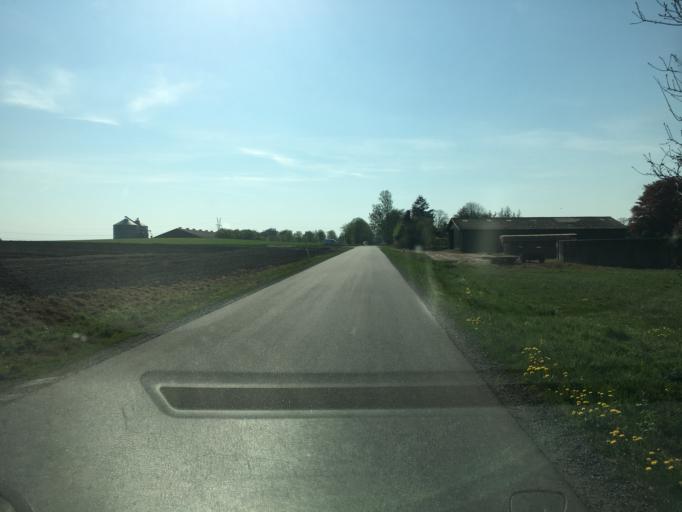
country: DK
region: South Denmark
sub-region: Haderslev Kommune
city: Vojens
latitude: 55.2324
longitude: 9.3499
